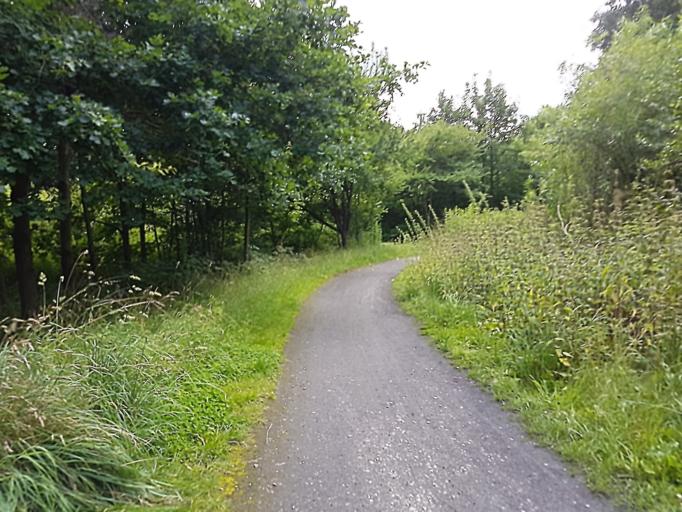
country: DK
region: Capital Region
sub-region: Fureso Kommune
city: Farum
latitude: 55.8036
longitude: 12.3787
